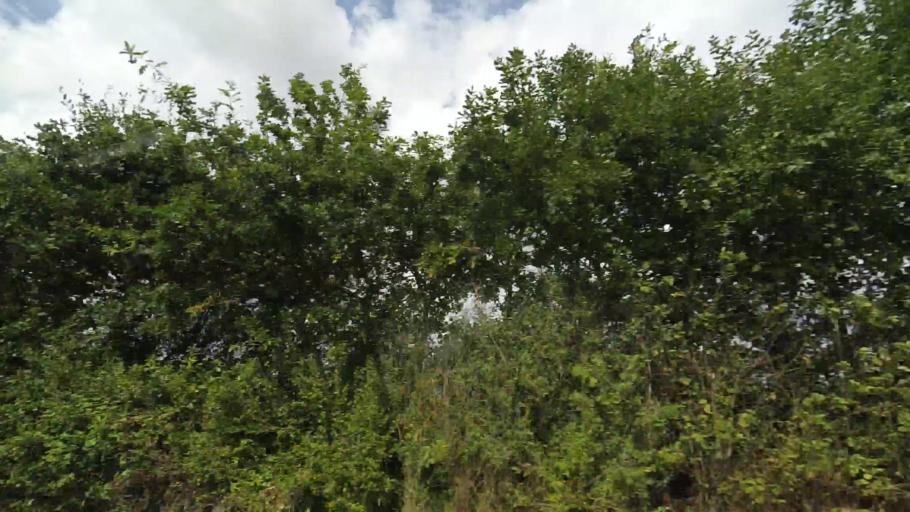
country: DK
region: Central Jutland
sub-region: Norddjurs Kommune
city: Allingabro
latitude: 56.5352
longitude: 10.3623
